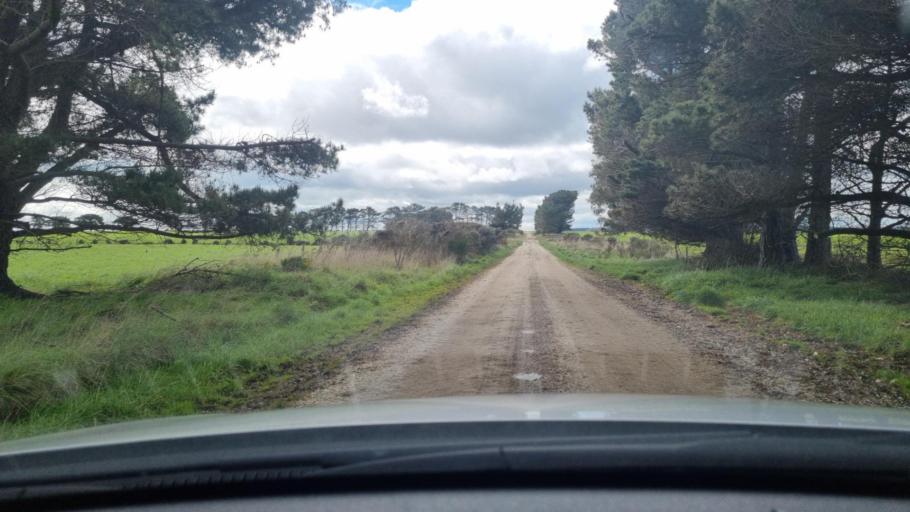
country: NZ
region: Southland
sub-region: Invercargill City
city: Bluff
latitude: -46.5701
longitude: 168.4995
